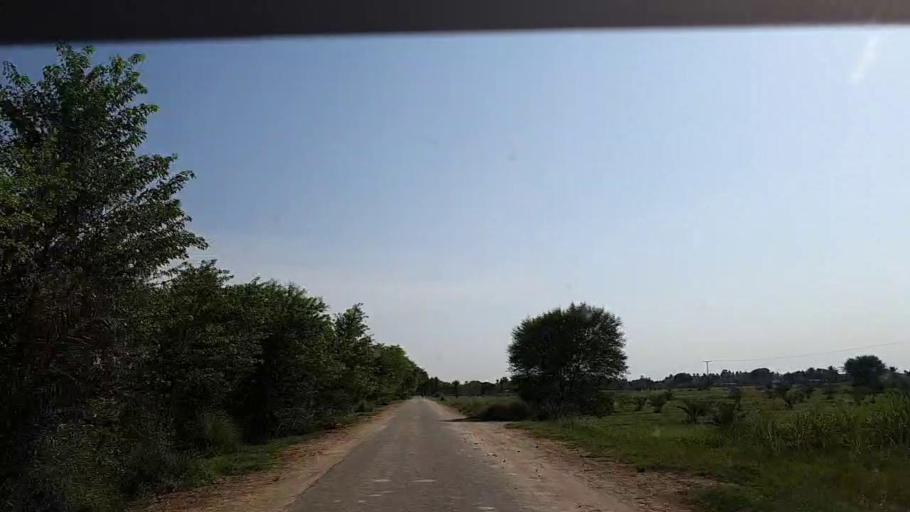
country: PK
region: Sindh
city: Adilpur
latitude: 27.9263
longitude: 69.2508
